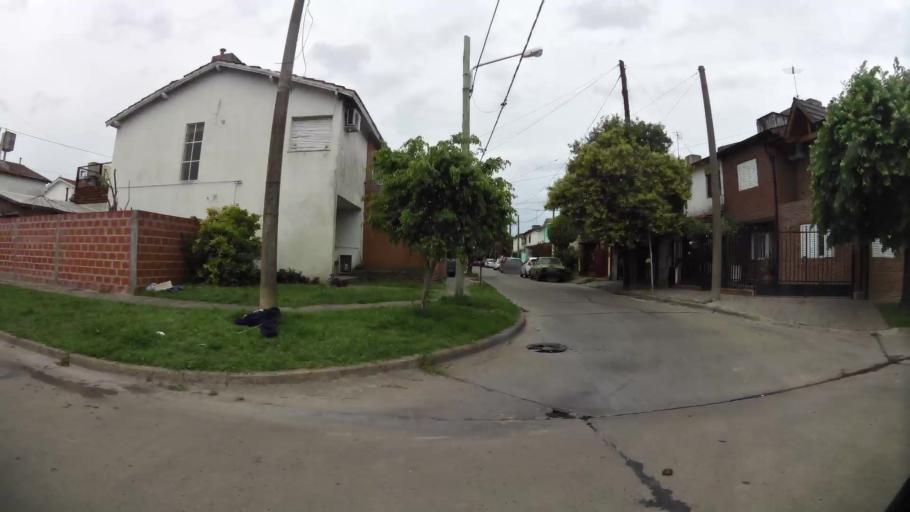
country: AR
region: Buenos Aires
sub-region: Partido de Campana
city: Campana
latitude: -34.1755
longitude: -58.9694
